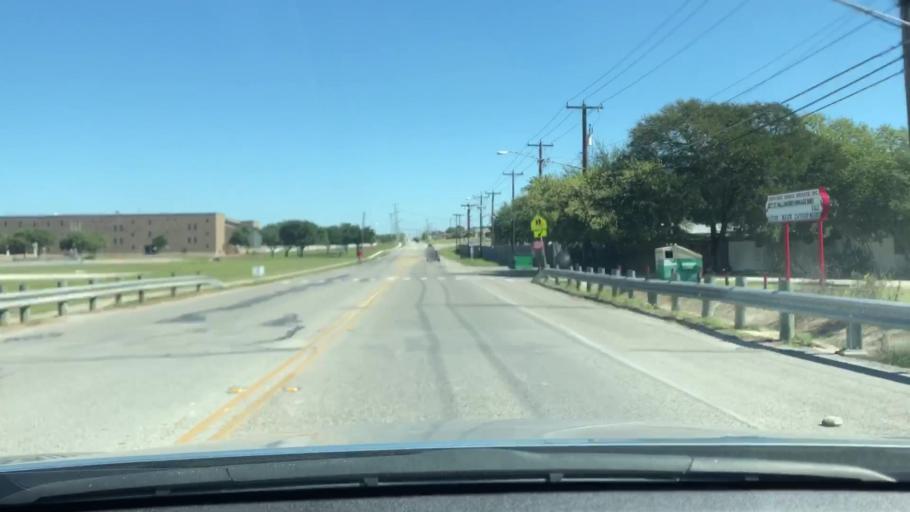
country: US
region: Texas
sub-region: Bexar County
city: Converse
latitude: 29.5091
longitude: -98.3002
